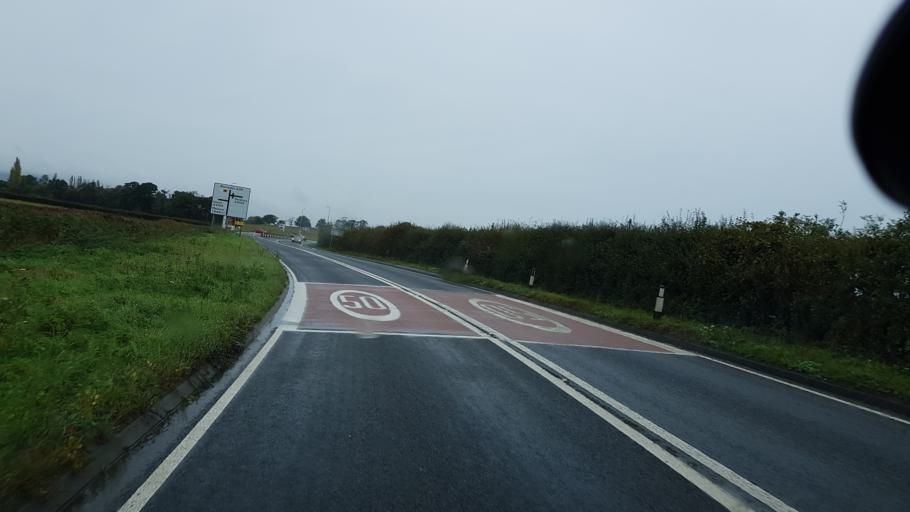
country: GB
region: England
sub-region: Worcestershire
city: Upton upon Severn
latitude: 52.0696
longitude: -2.1961
